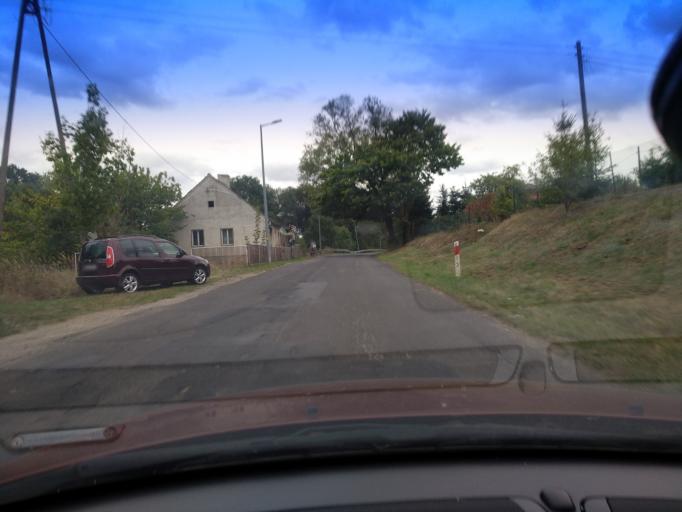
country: PL
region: Lower Silesian Voivodeship
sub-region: Powiat zgorzelecki
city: Zgorzelec
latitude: 51.1856
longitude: 15.0156
